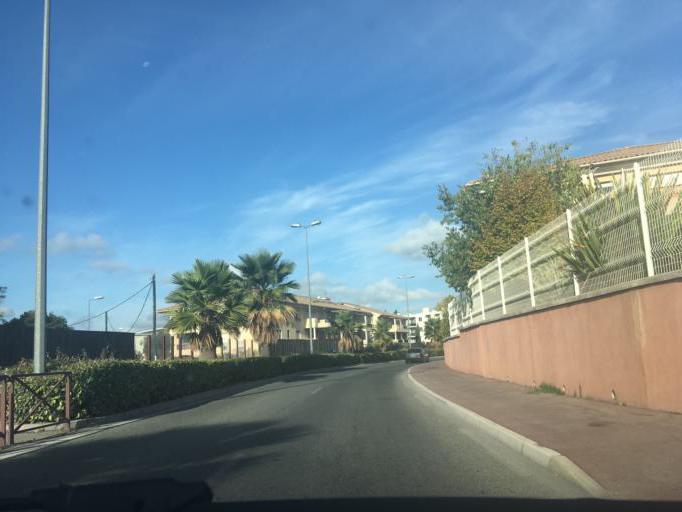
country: FR
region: Provence-Alpes-Cote d'Azur
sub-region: Departement du Var
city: Draguignan
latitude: 43.5299
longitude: 6.4674
